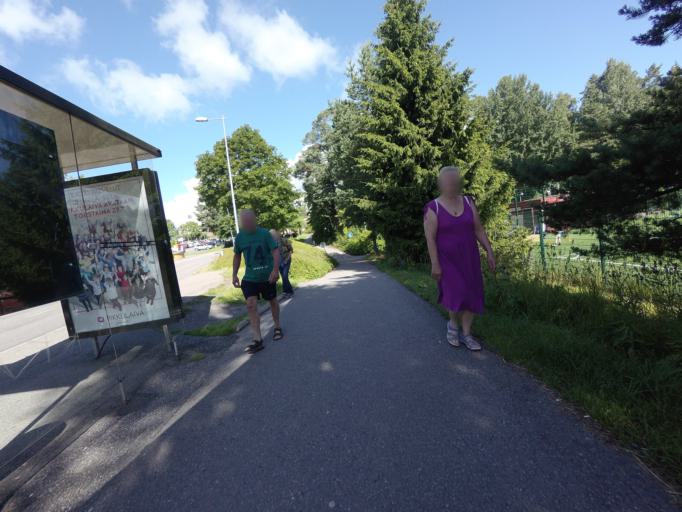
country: FI
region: Uusimaa
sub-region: Helsinki
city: Espoo
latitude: 60.1502
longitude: 24.6413
